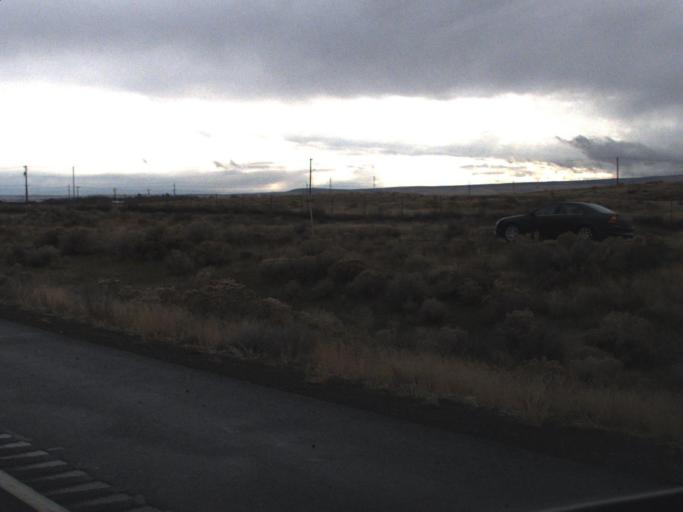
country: US
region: Washington
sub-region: Franklin County
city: Pasco
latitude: 46.2361
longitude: -119.0522
